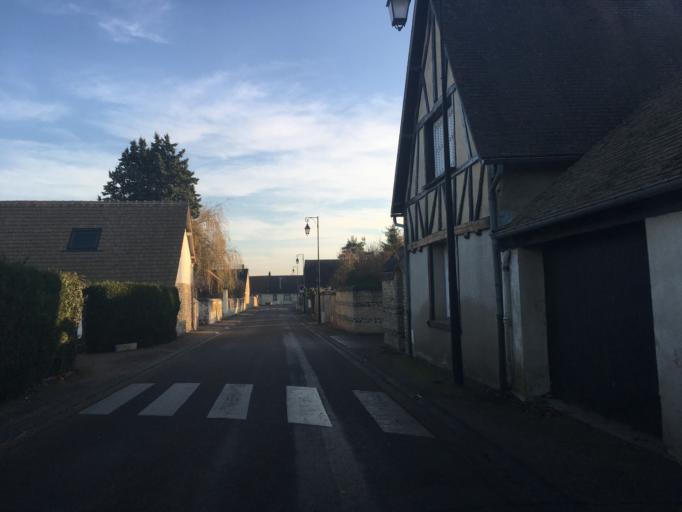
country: FR
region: Haute-Normandie
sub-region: Departement de l'Eure
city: Houlbec-Cocherel
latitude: 49.0527
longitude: 1.3012
